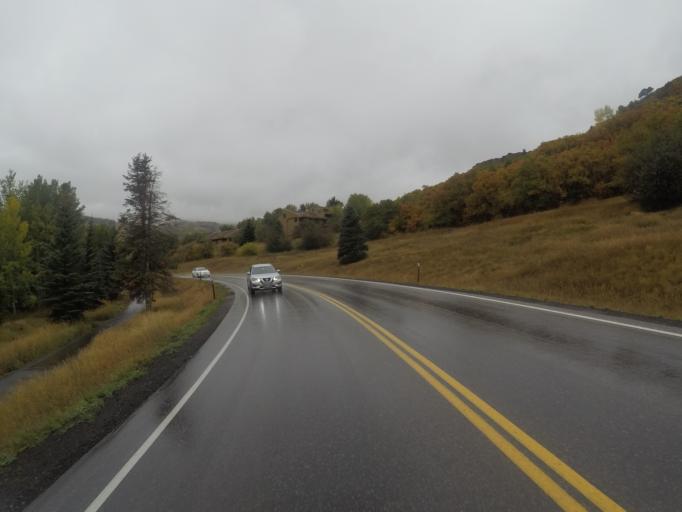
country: US
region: Colorado
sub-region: Pitkin County
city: Snowmass Village
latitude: 39.2153
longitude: -106.9382
